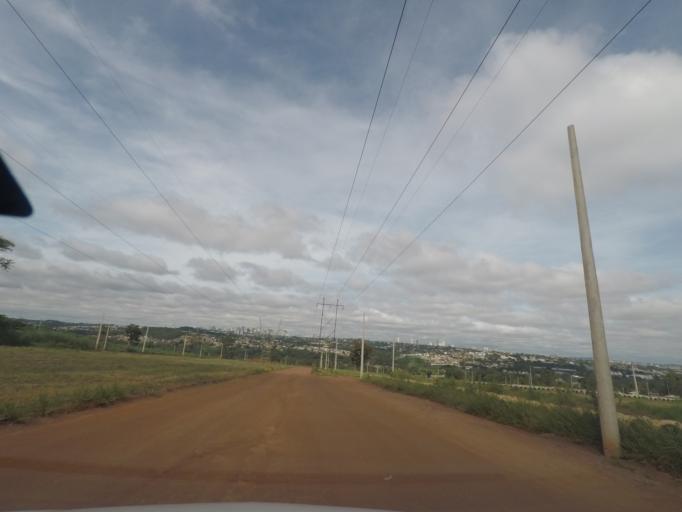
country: BR
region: Goias
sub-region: Goiania
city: Goiania
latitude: -16.6743
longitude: -49.1888
